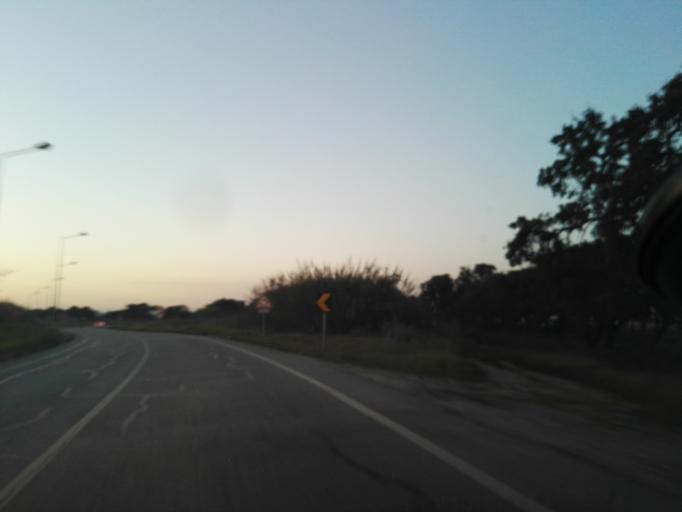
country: PT
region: Setubal
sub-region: Alcochete
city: Alcochete
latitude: 38.7250
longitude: -8.9056
